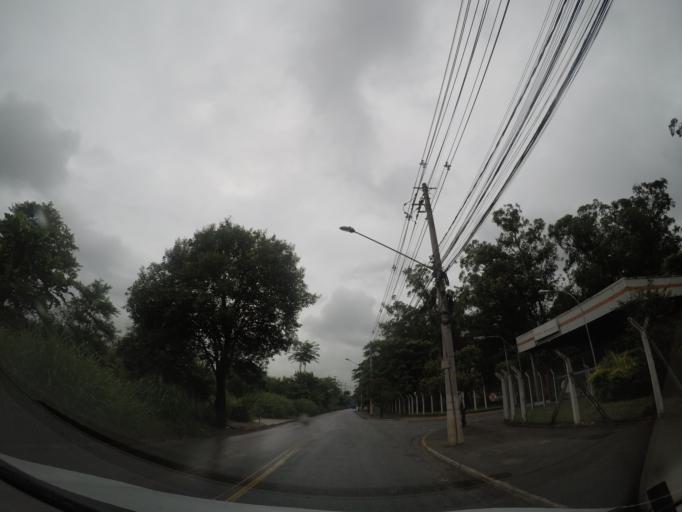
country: BR
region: Sao Paulo
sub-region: Guarulhos
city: Guarulhos
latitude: -23.4717
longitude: -46.4554
